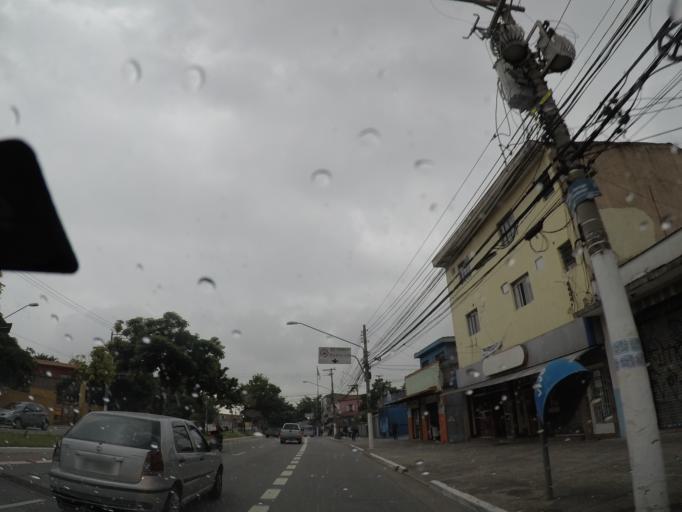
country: BR
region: Sao Paulo
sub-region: Diadema
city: Diadema
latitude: -23.6401
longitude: -46.6434
